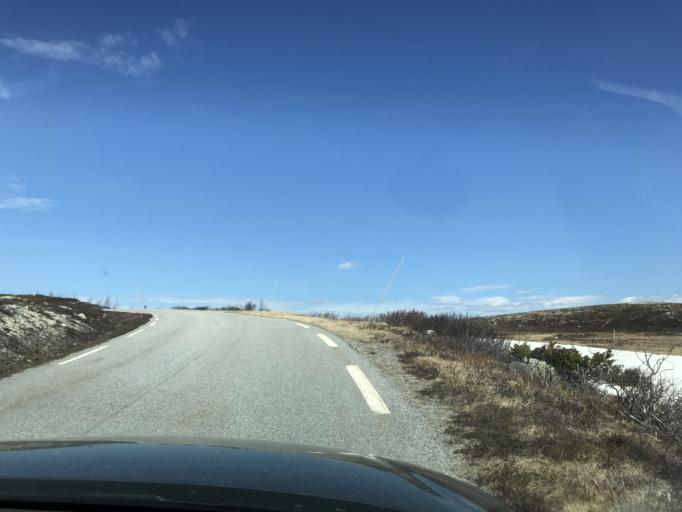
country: NO
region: Telemark
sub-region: Tinn
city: Rjukan
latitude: 59.8023
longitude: 8.7607
